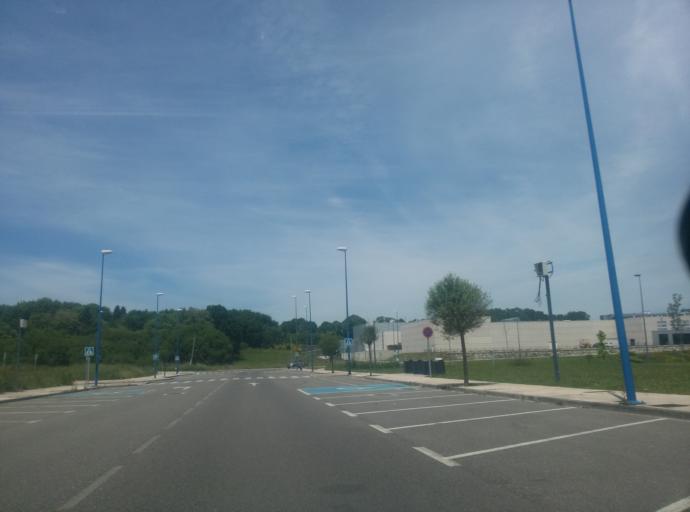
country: ES
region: Galicia
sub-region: Provincia de Lugo
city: Lugo
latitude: 43.0339
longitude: -7.5694
